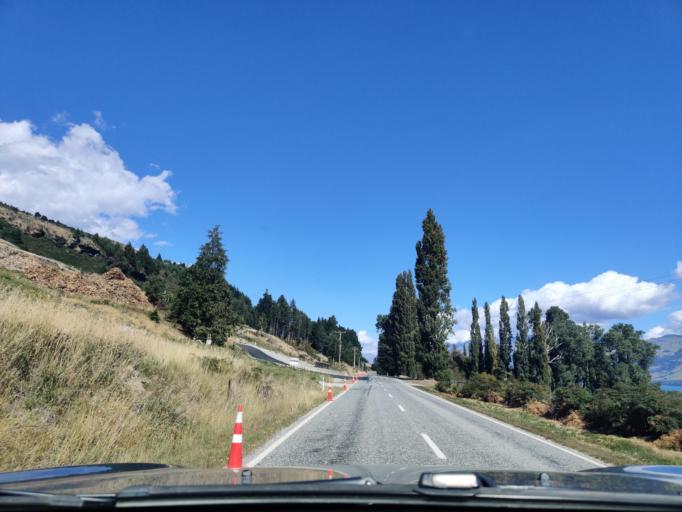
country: NZ
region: Otago
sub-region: Queenstown-Lakes District
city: Queenstown
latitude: -44.8198
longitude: 168.3986
